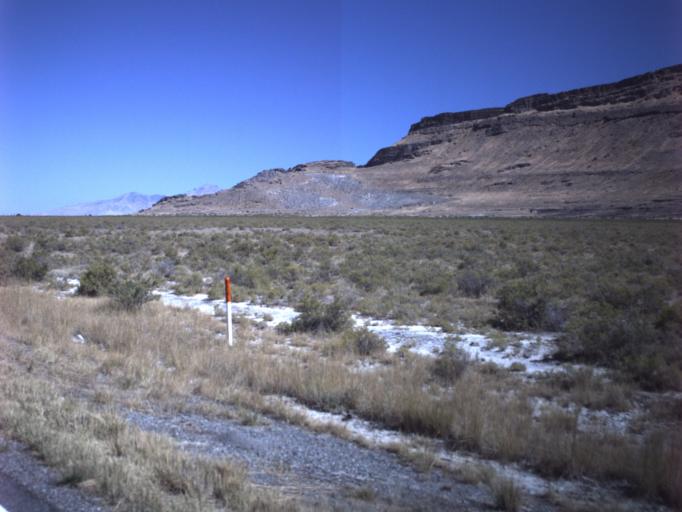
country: US
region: Utah
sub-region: Tooele County
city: Grantsville
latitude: 40.7286
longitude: -112.6580
